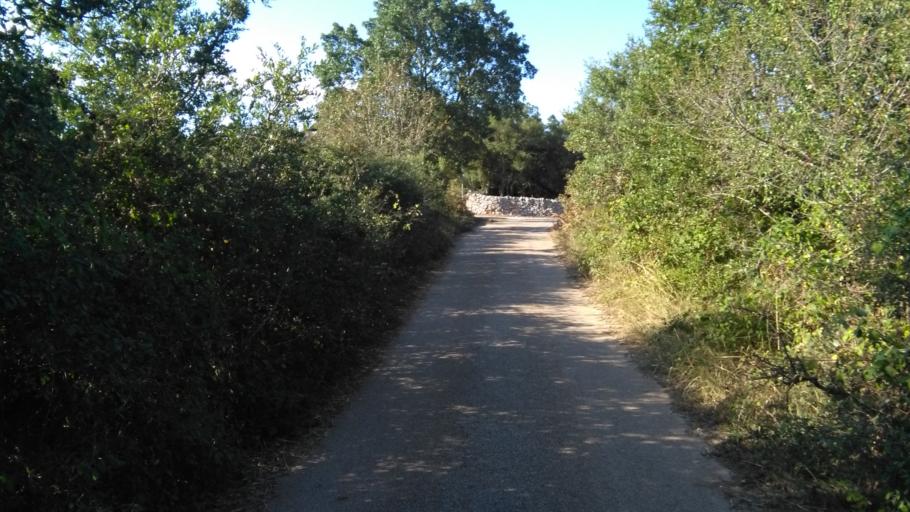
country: IT
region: Apulia
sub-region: Provincia di Bari
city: Putignano
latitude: 40.8200
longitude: 17.0595
